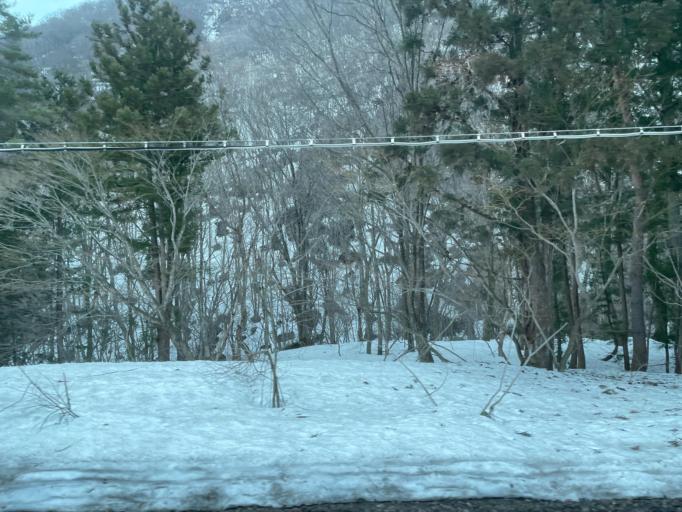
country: JP
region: Gunma
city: Numata
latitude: 36.7944
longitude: 138.9884
